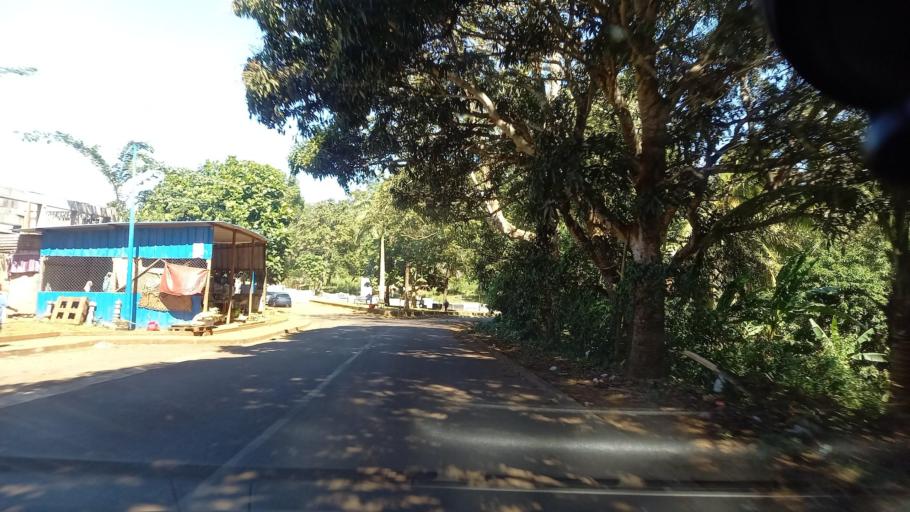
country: YT
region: Tsingoni
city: Tsingoni
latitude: -12.7861
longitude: 45.1409
